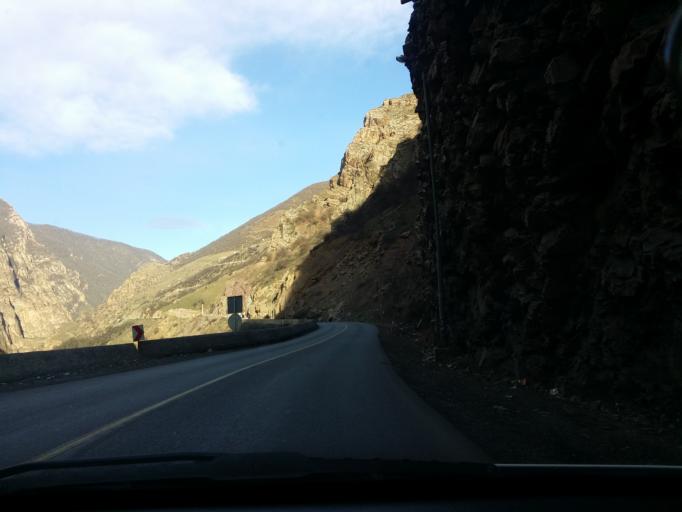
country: IR
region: Mazandaran
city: Chalus
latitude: 36.2615
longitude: 51.2664
